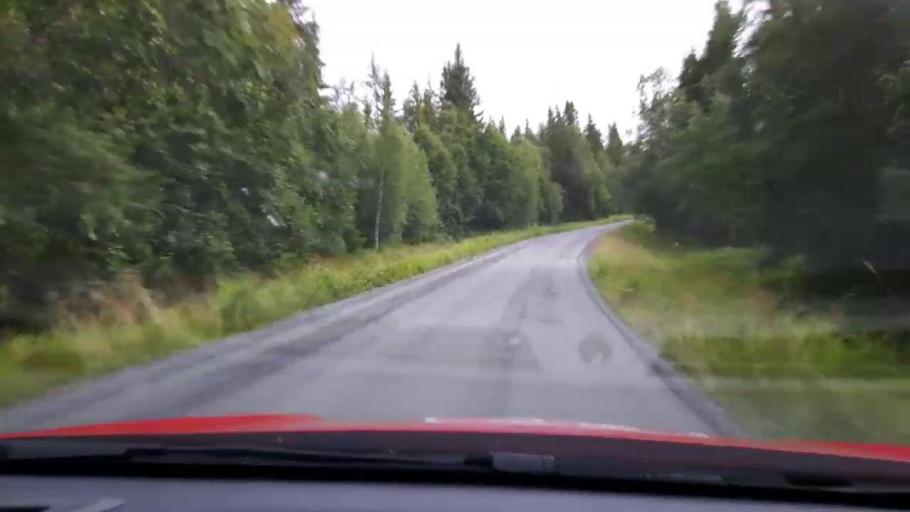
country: SE
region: Jaemtland
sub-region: Are Kommun
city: Are
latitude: 63.7392
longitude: 13.0151
